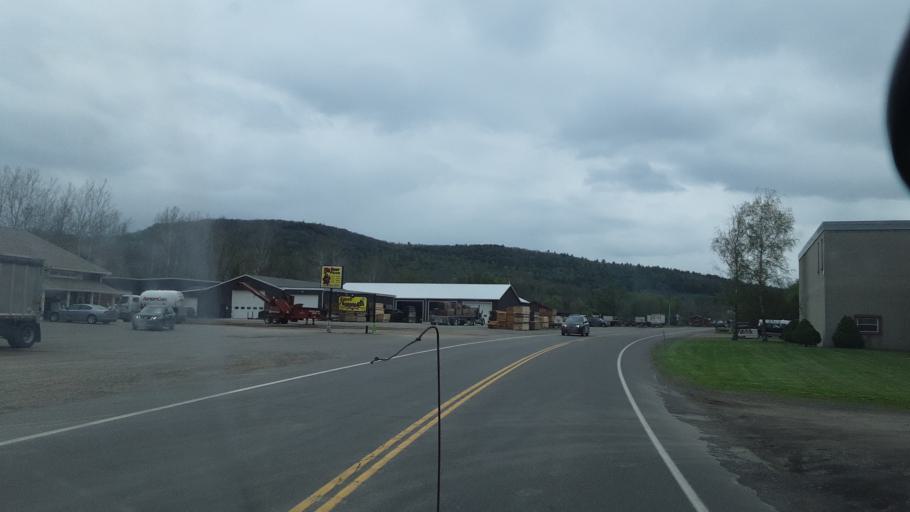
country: US
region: New York
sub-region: Steuben County
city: Addison
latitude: 42.0892
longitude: -77.2447
